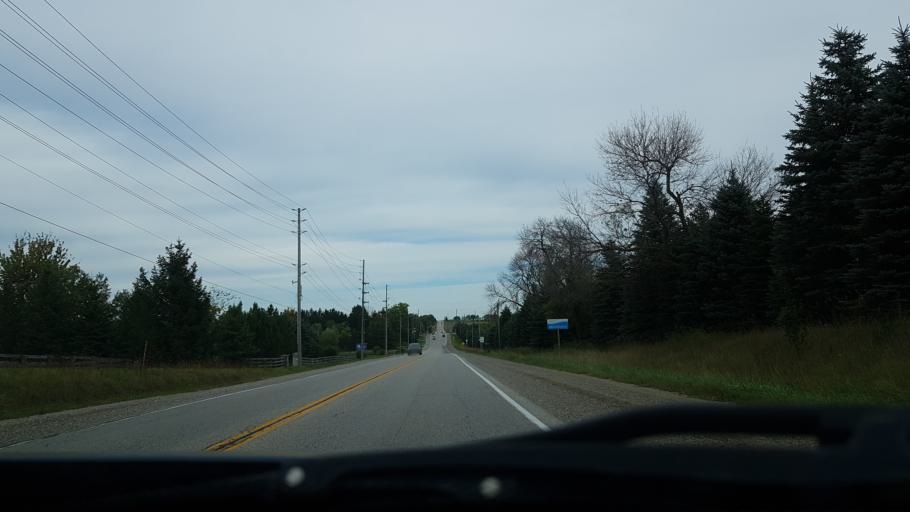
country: CA
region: Ontario
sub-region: Wellington County
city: Guelph
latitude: 43.6442
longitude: -80.1908
